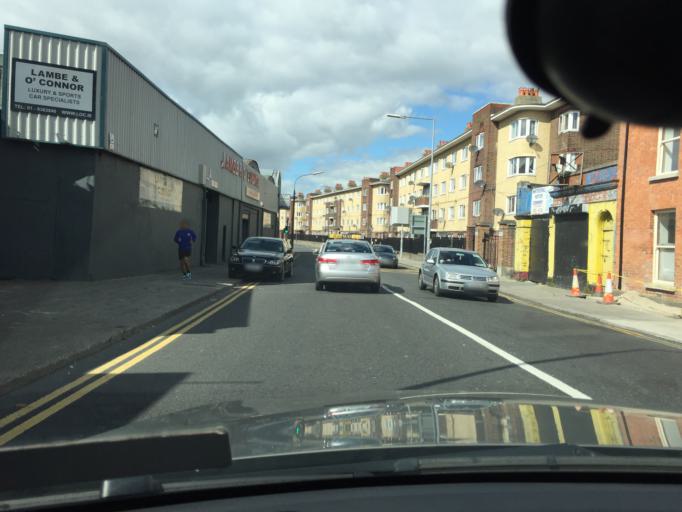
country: IE
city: Fairview
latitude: 53.3607
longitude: -6.2394
